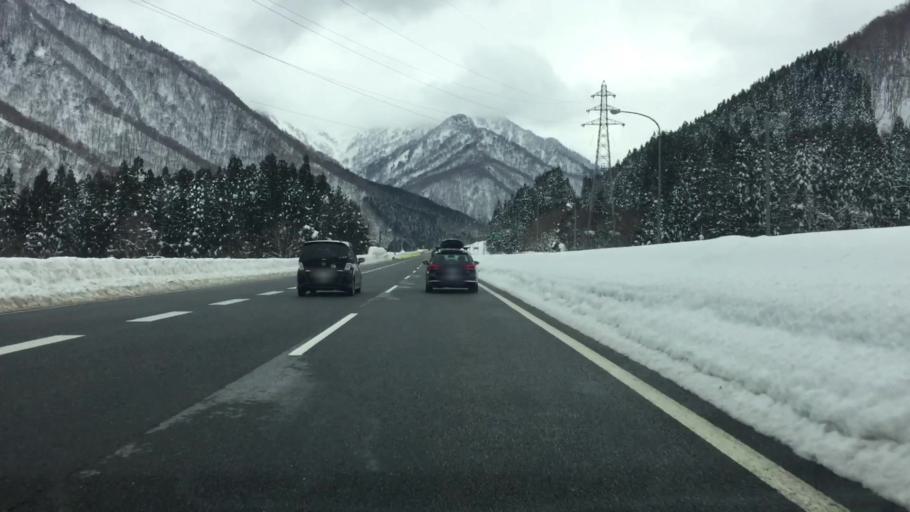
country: JP
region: Niigata
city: Shiozawa
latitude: 36.8806
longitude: 138.8550
